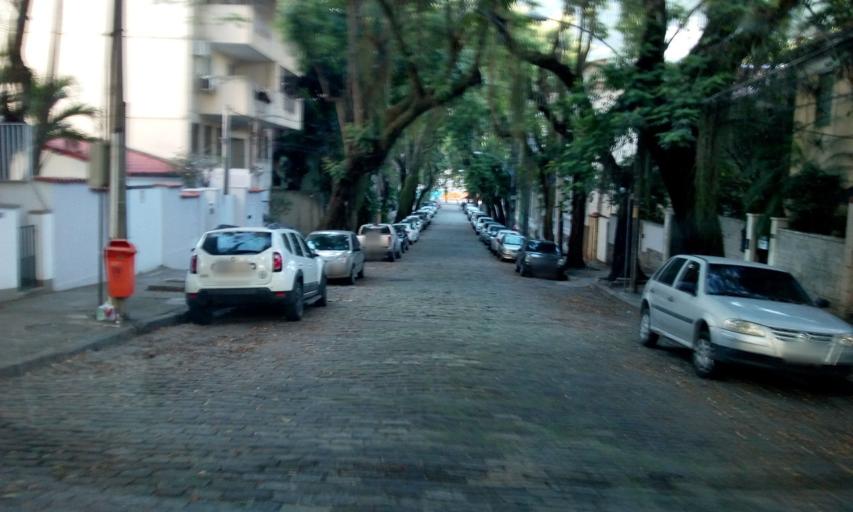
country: BR
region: Rio de Janeiro
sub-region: Rio De Janeiro
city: Rio de Janeiro
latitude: -22.9554
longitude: -43.2006
